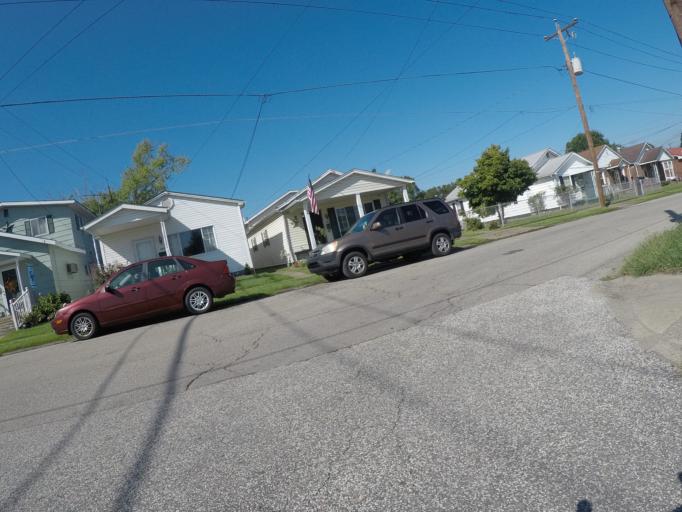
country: US
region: Ohio
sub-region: Lawrence County
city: Burlington
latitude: 38.4002
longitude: -82.4999
